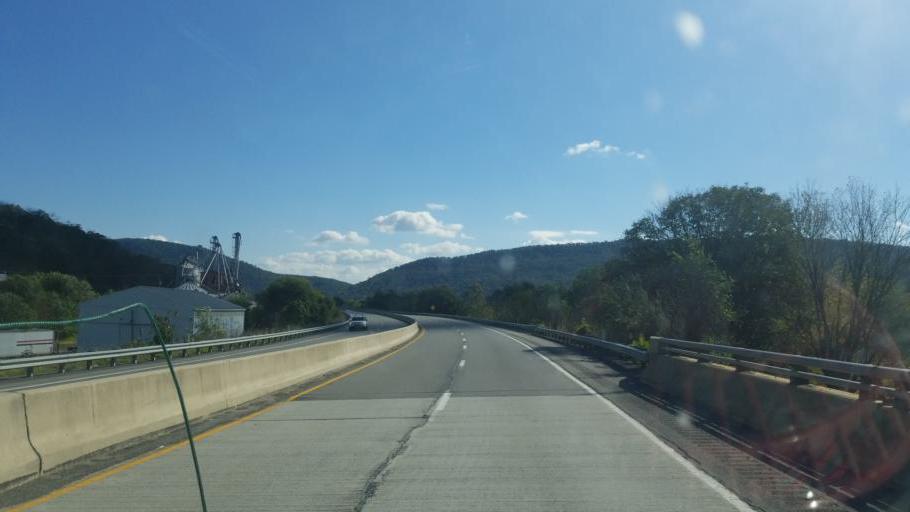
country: US
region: Pennsylvania
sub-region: Bedford County
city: Bedford
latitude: 40.0215
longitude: -78.5071
